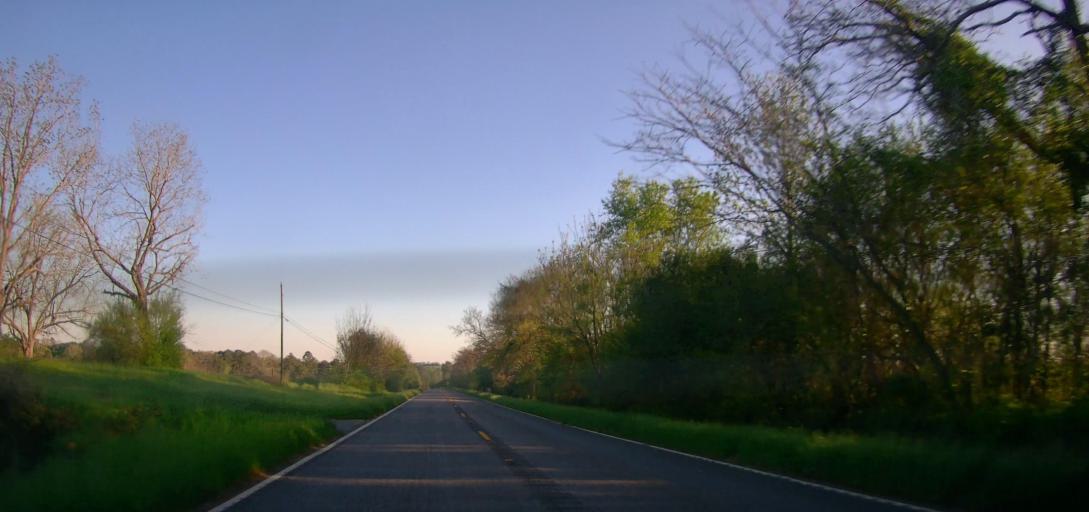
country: US
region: Georgia
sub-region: Marion County
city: Buena Vista
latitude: 32.3912
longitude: -84.4431
